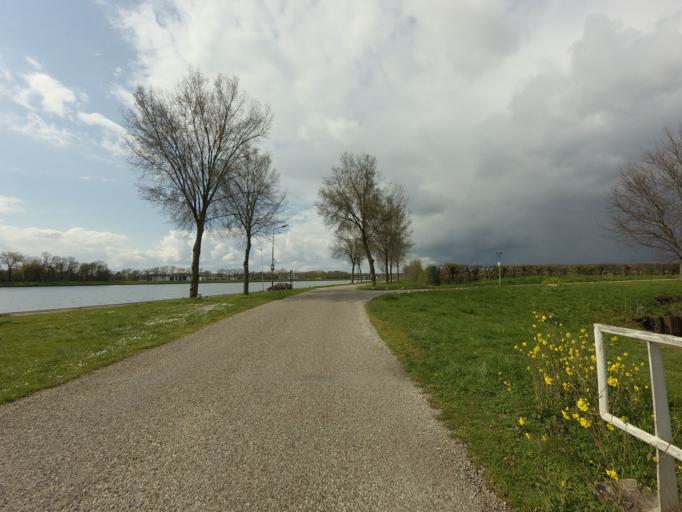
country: NL
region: Utrecht
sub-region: Gemeente Utrecht
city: Lunetten
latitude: 52.0384
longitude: 5.1147
